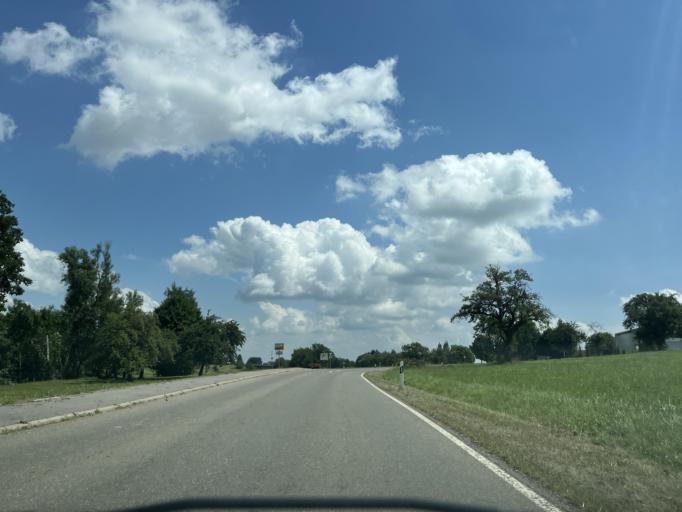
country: DE
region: Baden-Wuerttemberg
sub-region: Tuebingen Region
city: Messkirch
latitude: 47.9942
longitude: 9.0752
